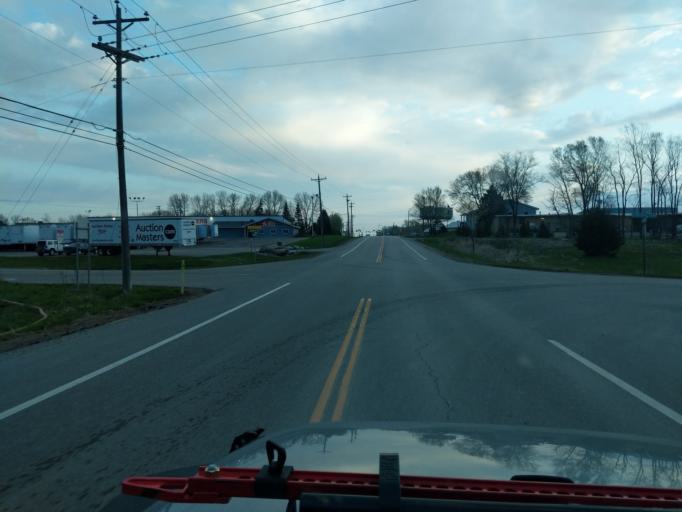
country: US
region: Minnesota
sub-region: Hennepin County
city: Rogers
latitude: 45.1657
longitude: -93.5214
